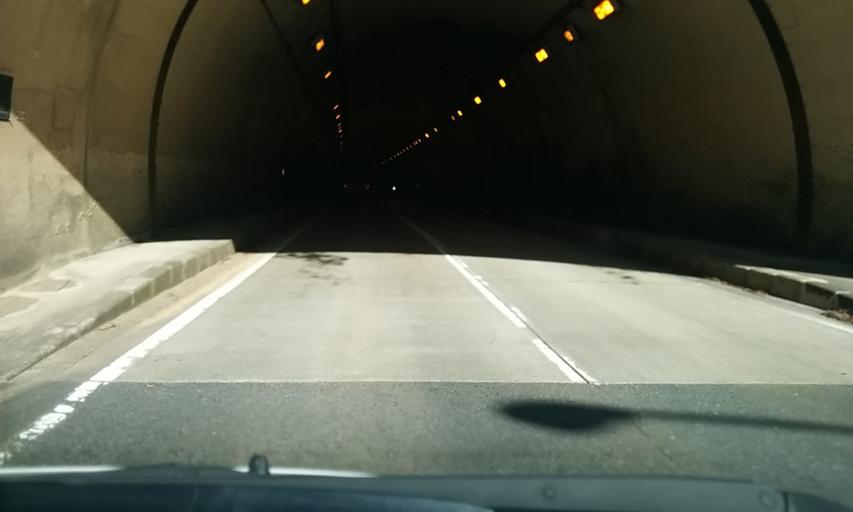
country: JP
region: Kyoto
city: Kameoka
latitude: 35.2212
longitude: 135.5716
